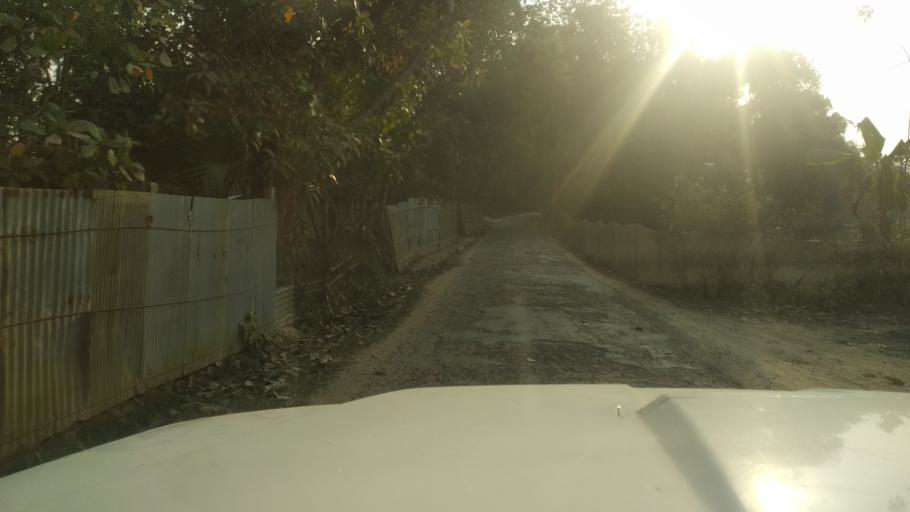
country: IN
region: Tripura
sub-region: West Tripura
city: Sonamura
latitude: 23.3262
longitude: 91.2998
